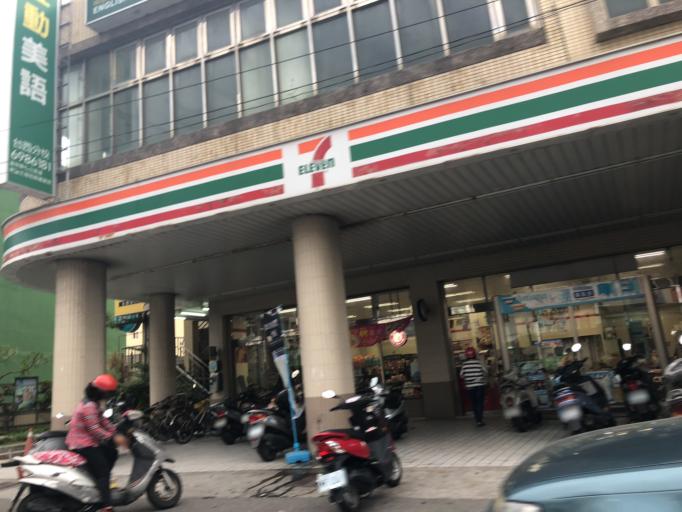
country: TW
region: Taiwan
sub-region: Chiayi
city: Taibao
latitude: 23.6996
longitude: 120.1986
